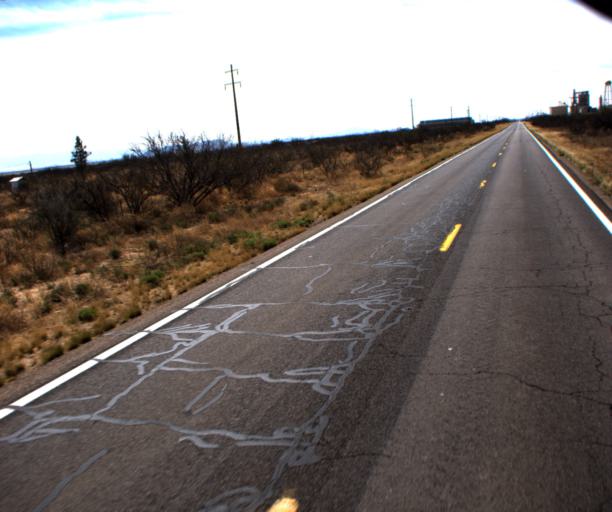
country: US
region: Arizona
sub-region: Cochise County
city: Willcox
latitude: 32.0721
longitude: -109.8972
